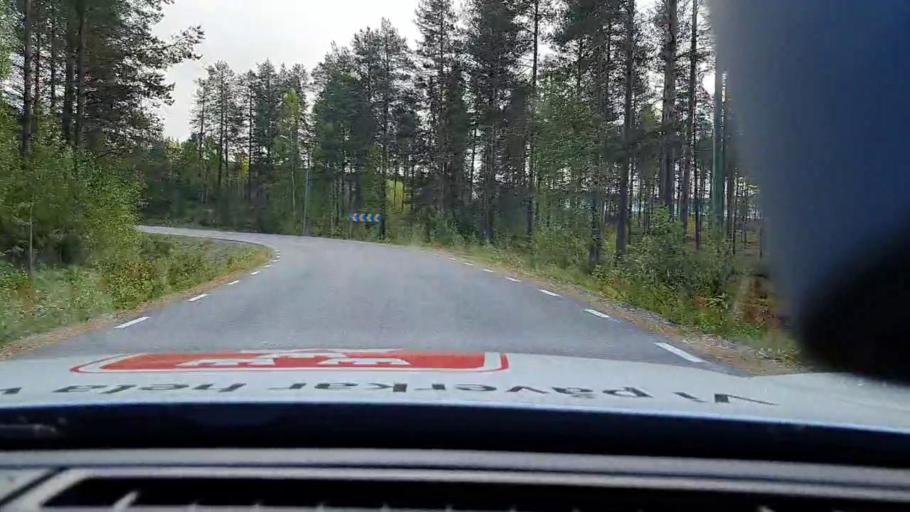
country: SE
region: Vaesterbotten
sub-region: Skelleftea Kommun
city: Langsele
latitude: 64.9395
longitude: 20.0038
